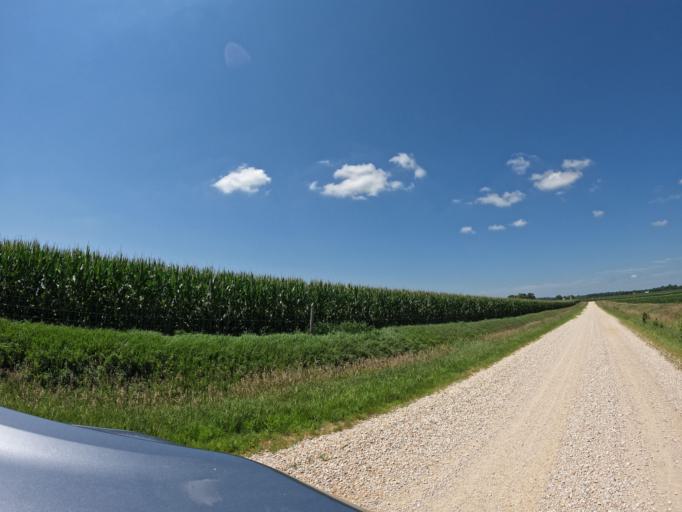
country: US
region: Iowa
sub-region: Clinton County
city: De Witt
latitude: 41.7793
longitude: -90.4097
